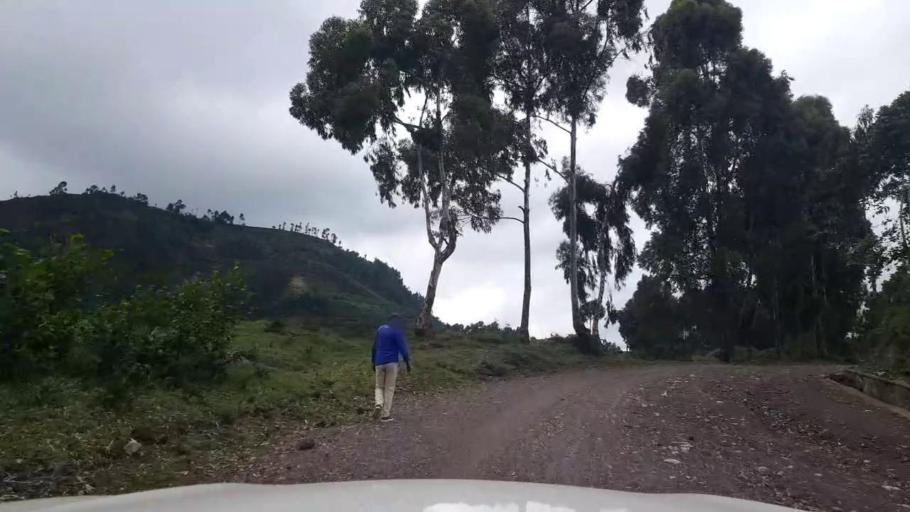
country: RW
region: Northern Province
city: Musanze
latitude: -1.5885
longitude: 29.4702
